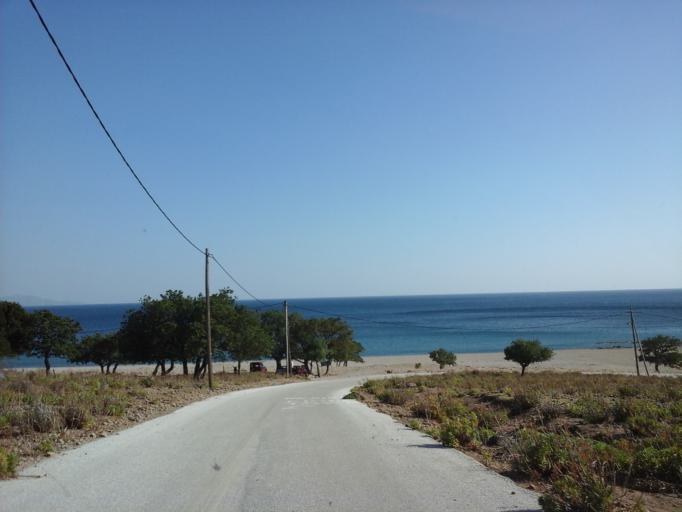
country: GR
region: East Macedonia and Thrace
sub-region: Nomos Evrou
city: Samothraki
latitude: 40.3972
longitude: 25.5810
